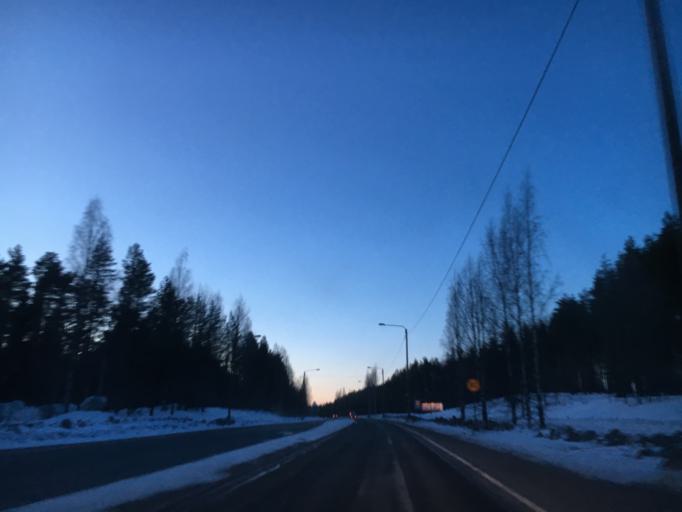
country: FI
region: Kainuu
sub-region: Kajaani
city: Kajaani
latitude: 64.1963
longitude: 27.7508
